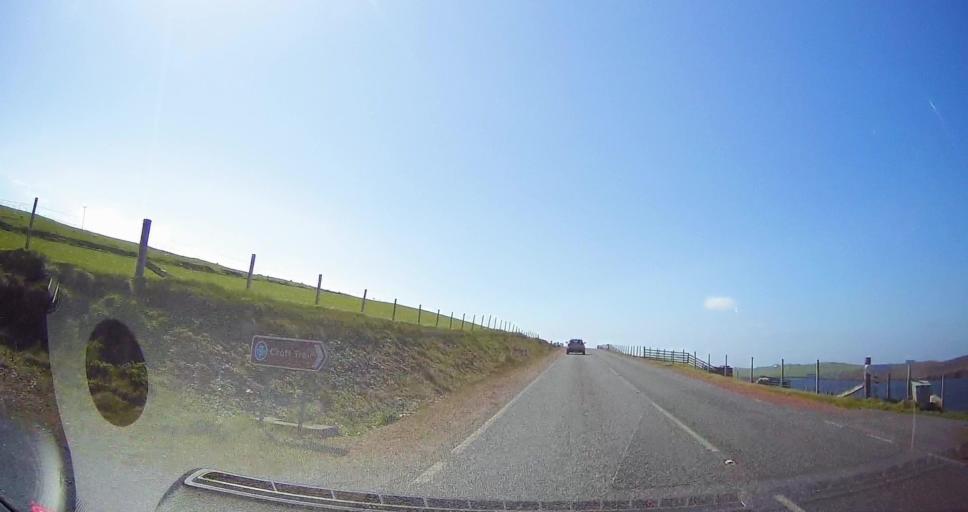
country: GB
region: Scotland
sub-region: Shetland Islands
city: Sandwick
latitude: 60.1157
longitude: -1.2932
